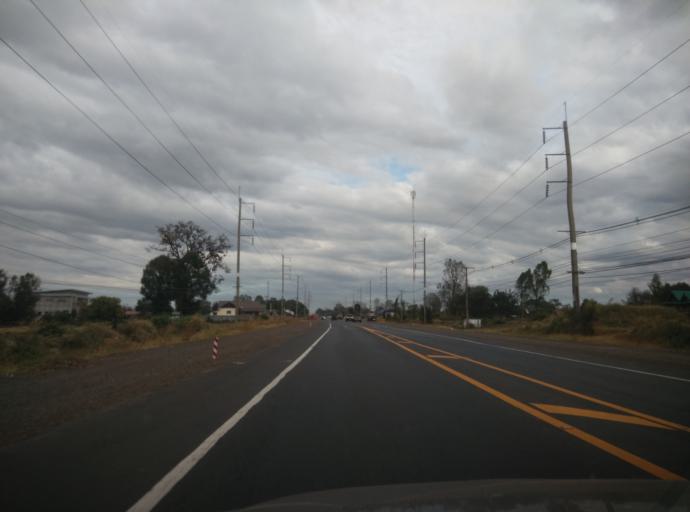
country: TH
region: Sisaket
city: Uthumphon Phisai
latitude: 15.1528
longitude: 104.2016
